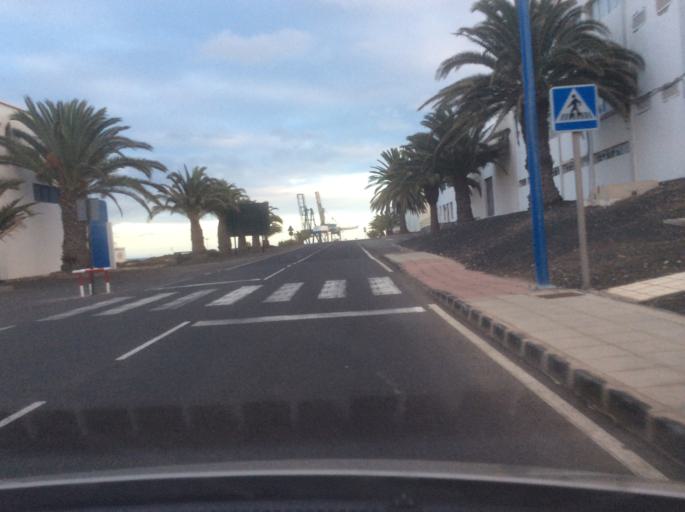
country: ES
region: Canary Islands
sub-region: Provincia de Las Palmas
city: Arrecife
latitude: 28.9748
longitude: -13.5336
